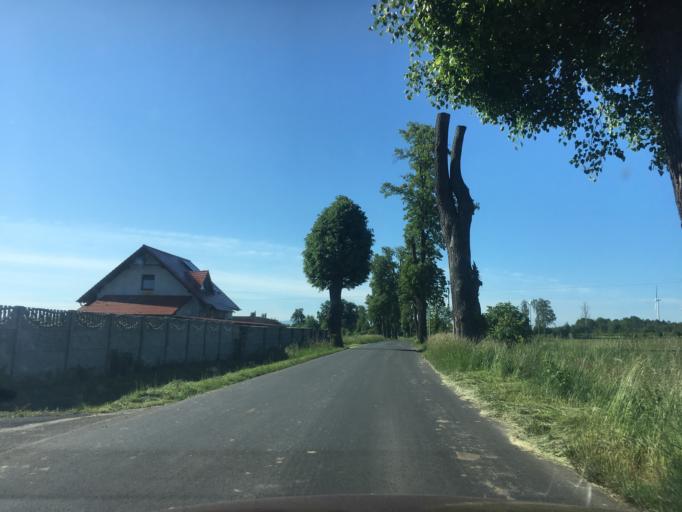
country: PL
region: Lower Silesian Voivodeship
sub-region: Powiat zgorzelecki
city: Sulikow
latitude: 51.1045
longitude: 15.0366
